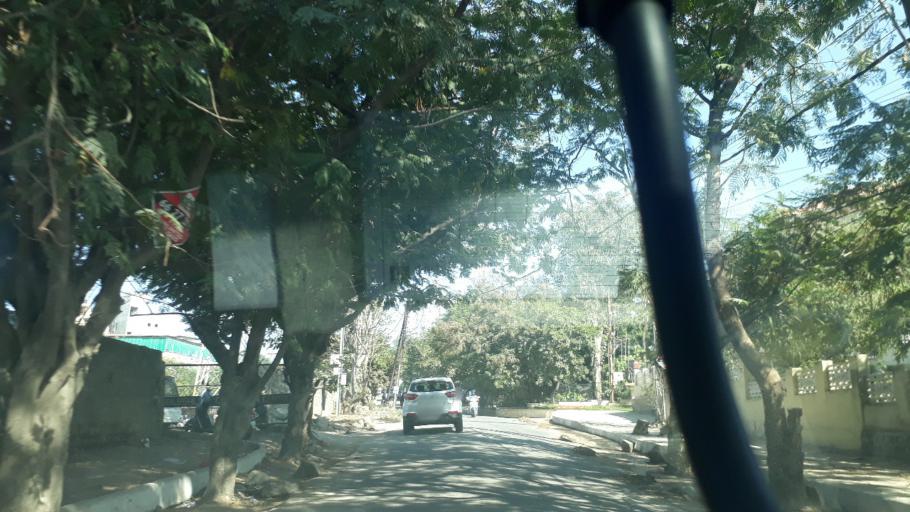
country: IN
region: Telangana
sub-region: Rangareddi
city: Kukatpalli
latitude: 17.4266
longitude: 78.4008
